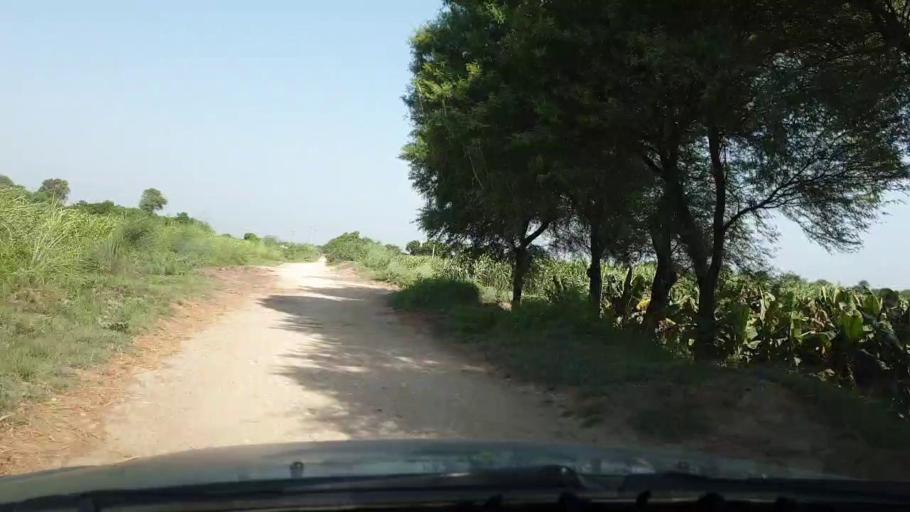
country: PK
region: Sindh
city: Matli
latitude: 25.0807
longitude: 68.6149
